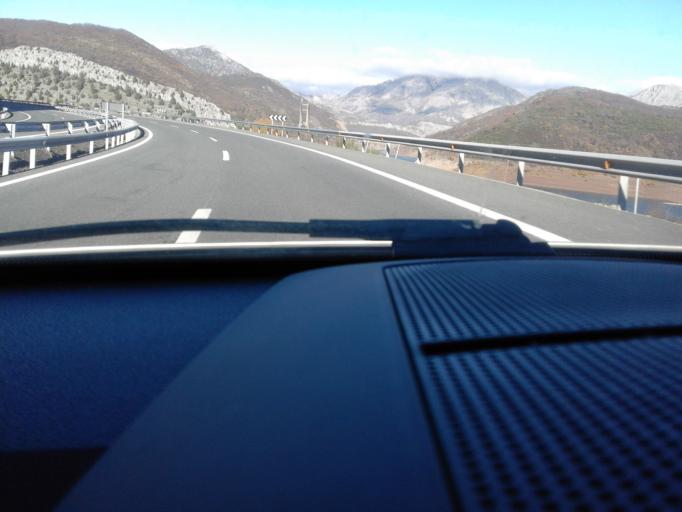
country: ES
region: Castille and Leon
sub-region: Provincia de Leon
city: Sena de Luna
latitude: 42.8781
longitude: -5.8808
